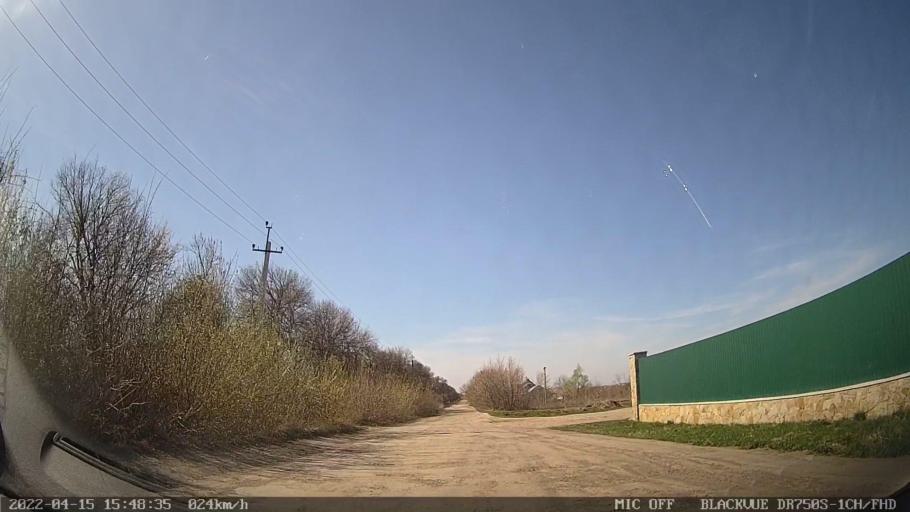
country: MD
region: Raionul Ocnita
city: Otaci
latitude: 48.3874
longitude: 27.9063
